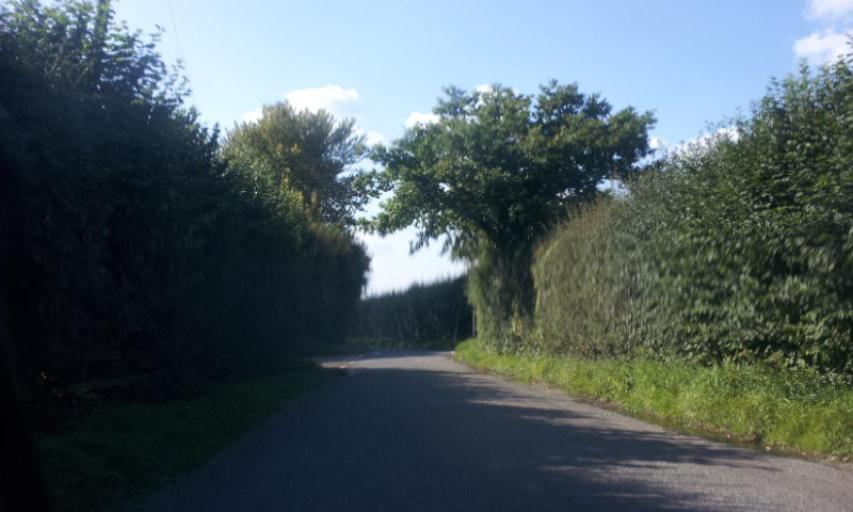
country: GB
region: England
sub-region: Kent
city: Hadlow
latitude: 51.2222
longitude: 0.3490
